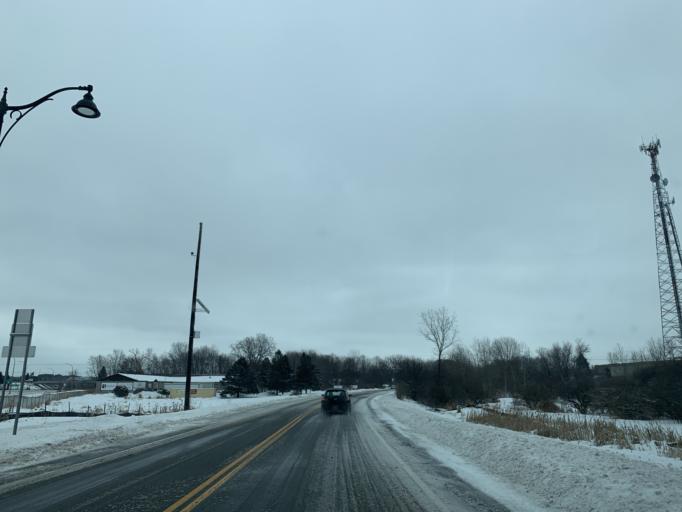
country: US
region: Minnesota
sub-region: Ramsey County
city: North Saint Paul
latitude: 45.0275
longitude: -92.9688
